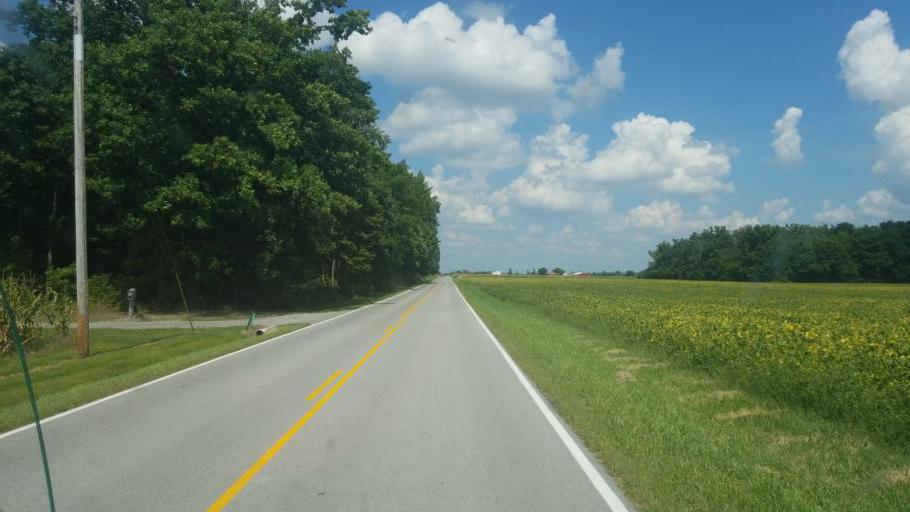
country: US
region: Ohio
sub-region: Hancock County
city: Arlington
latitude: 40.8663
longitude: -83.7273
